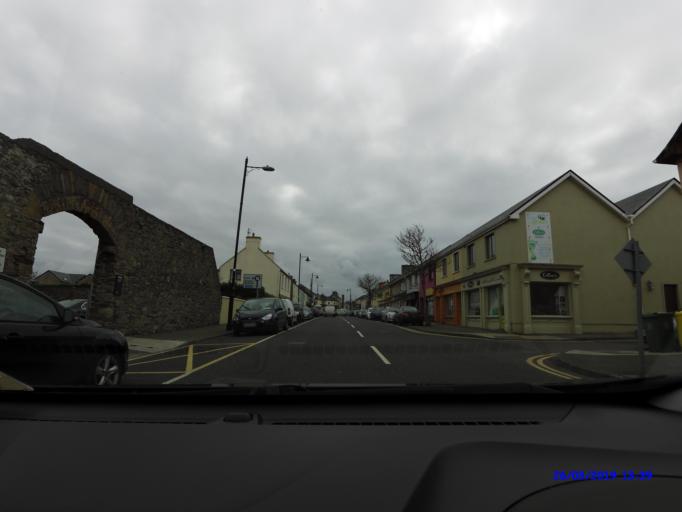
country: IE
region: Connaught
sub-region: Maigh Eo
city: Belmullet
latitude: 54.2251
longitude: -9.9880
